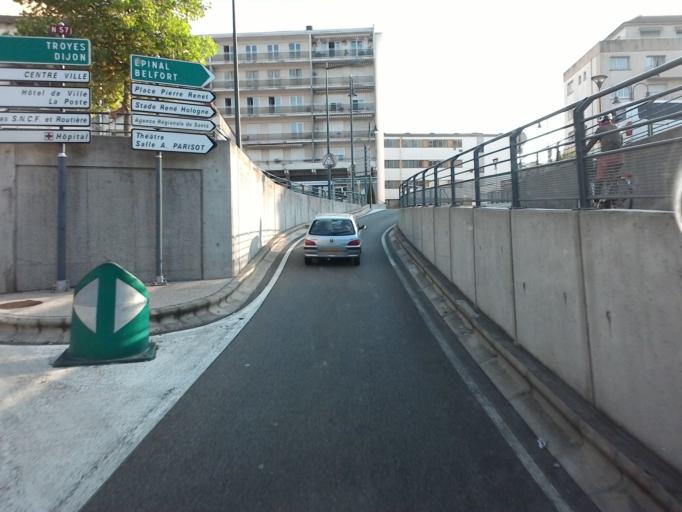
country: FR
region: Franche-Comte
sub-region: Departement de la Haute-Saone
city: Navenne
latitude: 47.6172
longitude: 6.1543
